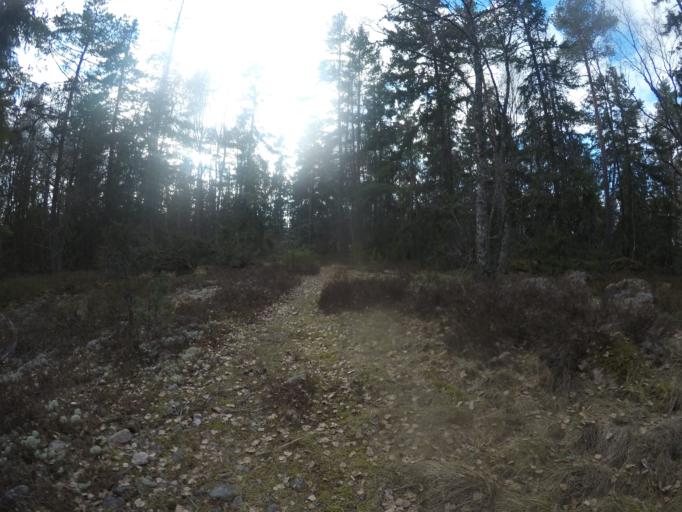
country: SE
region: Soedermanland
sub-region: Eskilstuna Kommun
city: Hallbybrunn
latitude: 59.3887
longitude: 16.3968
